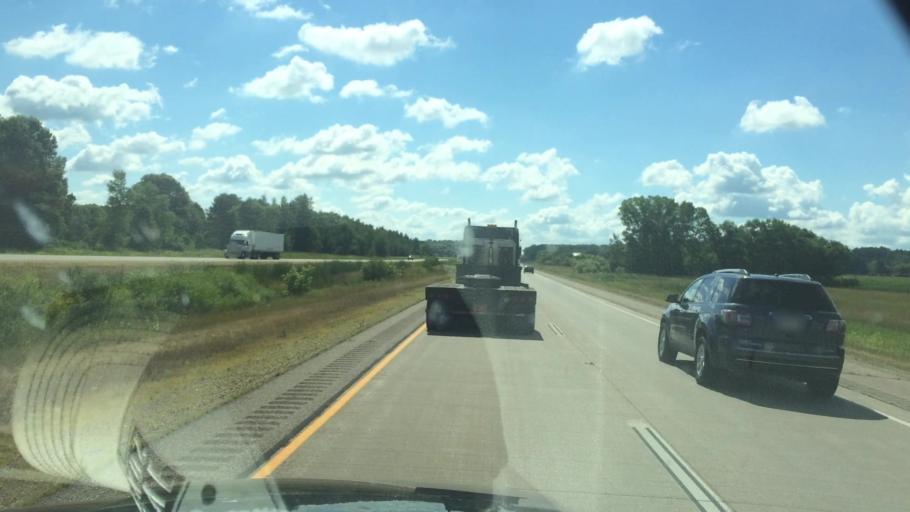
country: US
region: Wisconsin
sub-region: Portage County
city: Amherst
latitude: 44.3979
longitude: -89.2110
